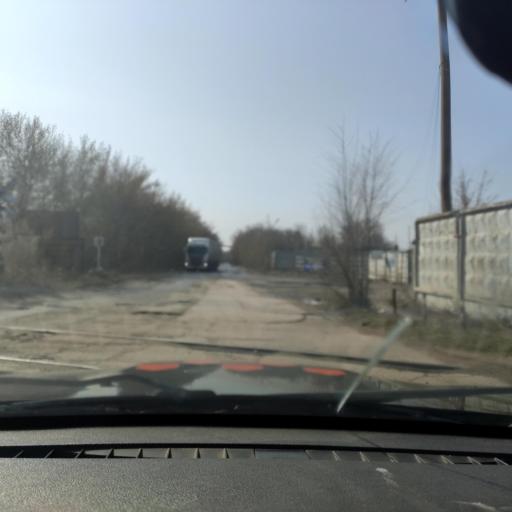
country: RU
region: Samara
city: Tol'yatti
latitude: 53.5679
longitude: 49.2987
